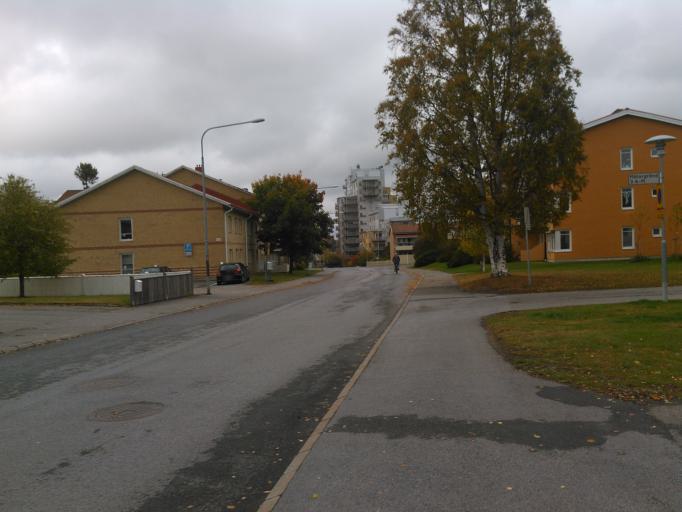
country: SE
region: Vaesterbotten
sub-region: Umea Kommun
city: Umea
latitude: 63.8215
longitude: 20.2486
